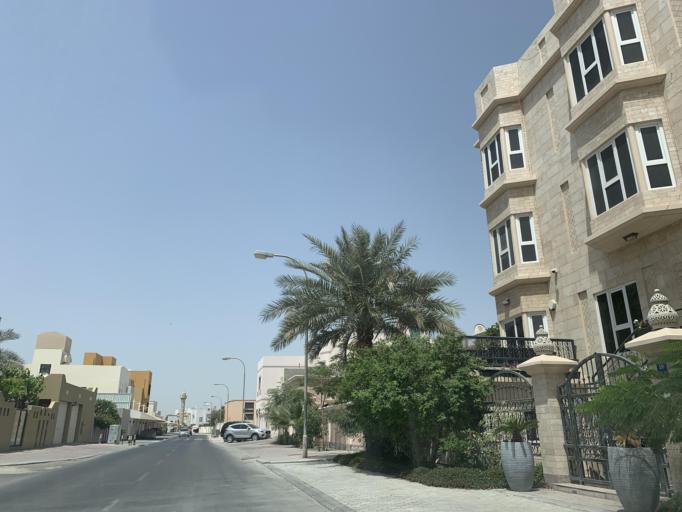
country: BH
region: Northern
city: Sitrah
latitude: 26.1586
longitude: 50.5842
